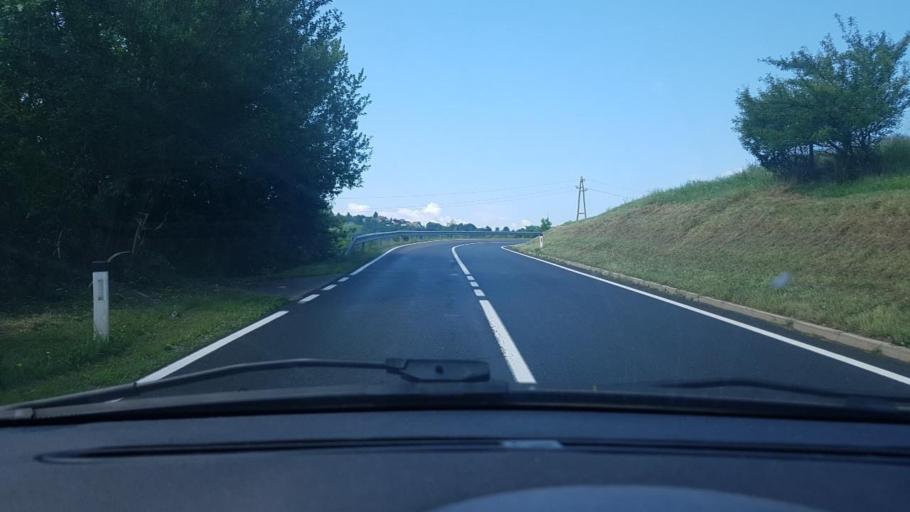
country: SI
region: Sentilj
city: Selnica ob Muri
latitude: 46.6889
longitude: 15.6827
